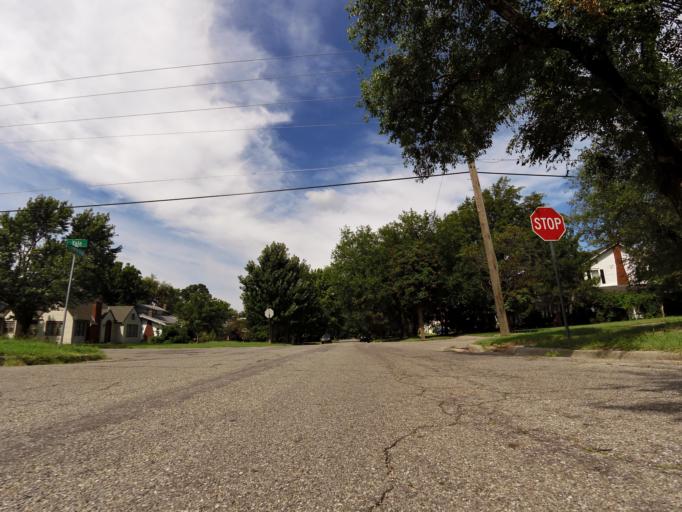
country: US
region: Kansas
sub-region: Sedgwick County
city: Wichita
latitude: 37.6992
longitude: -97.2934
